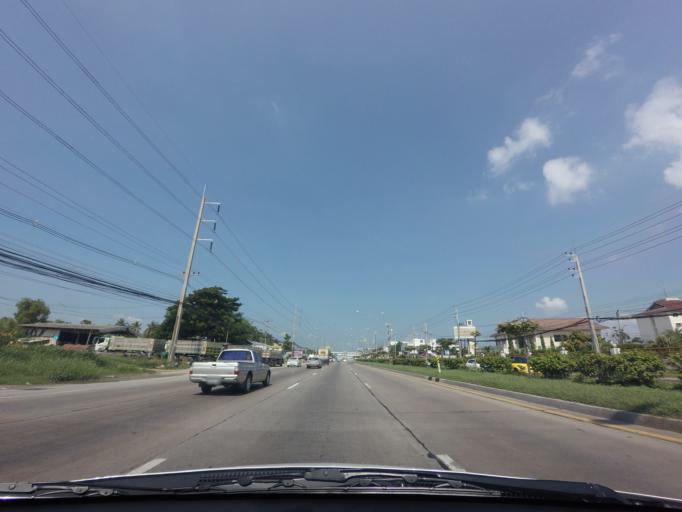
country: TH
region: Nakhon Pathom
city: Nakhon Chai Si
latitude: 13.7817
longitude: 100.1757
